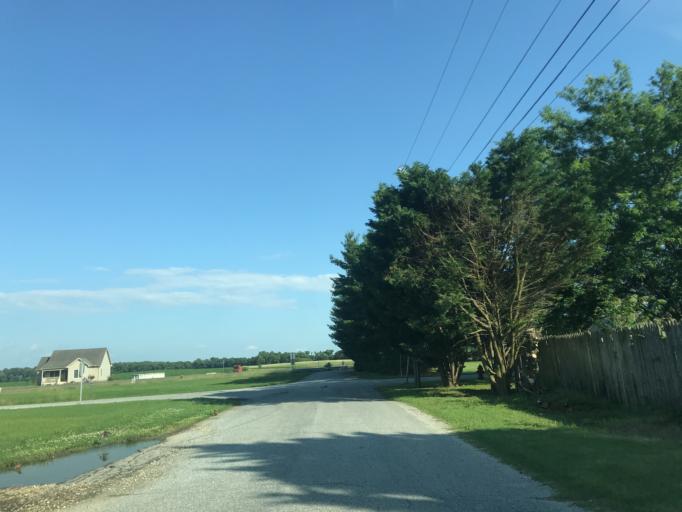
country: US
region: Maryland
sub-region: Wicomico County
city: Hebron
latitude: 38.5365
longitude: -75.7124
